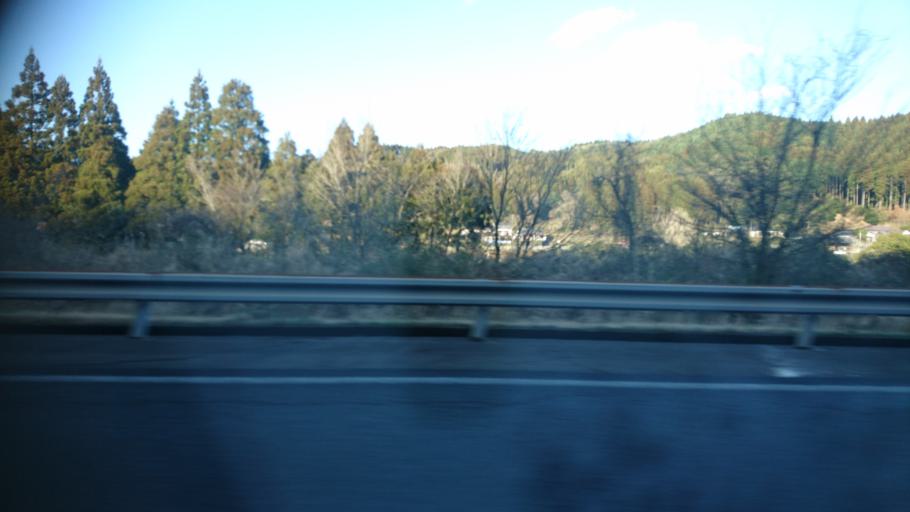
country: JP
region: Miyazaki
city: Miyakonojo
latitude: 31.7931
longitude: 131.1775
